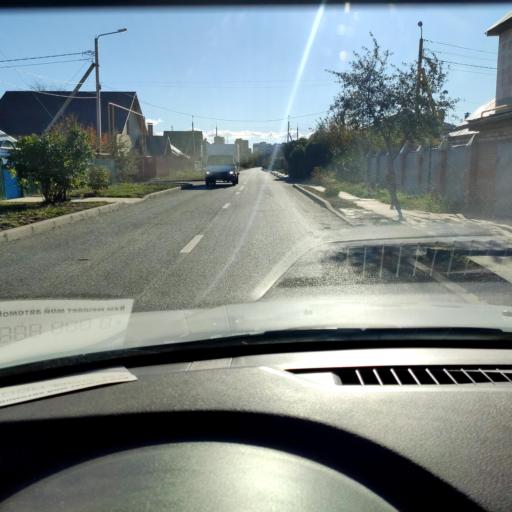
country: RU
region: Samara
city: Tol'yatti
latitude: 53.5302
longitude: 49.4220
